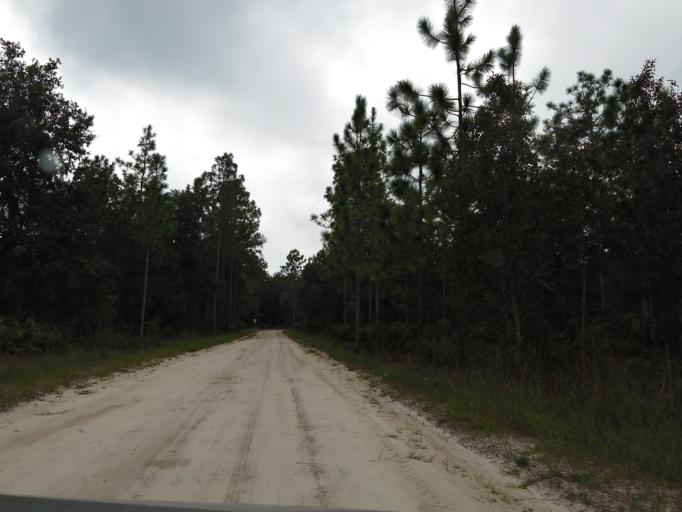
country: US
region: Florida
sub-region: Clay County
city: Middleburg
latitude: 30.1303
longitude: -81.9493
